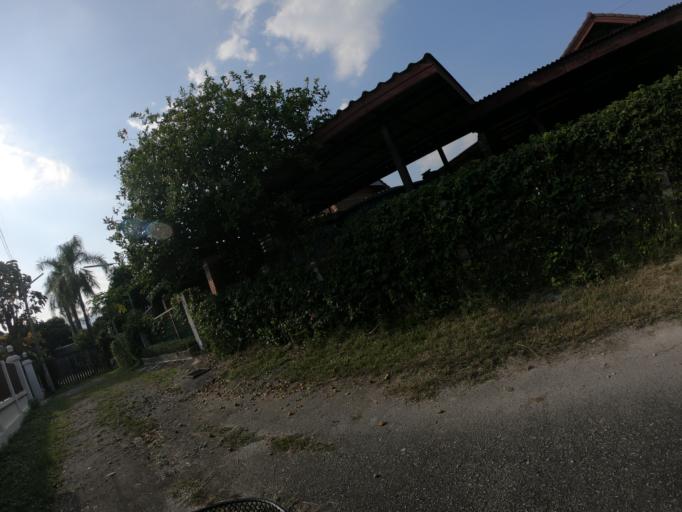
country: TH
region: Chiang Mai
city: Chiang Mai
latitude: 18.8330
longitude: 98.9851
